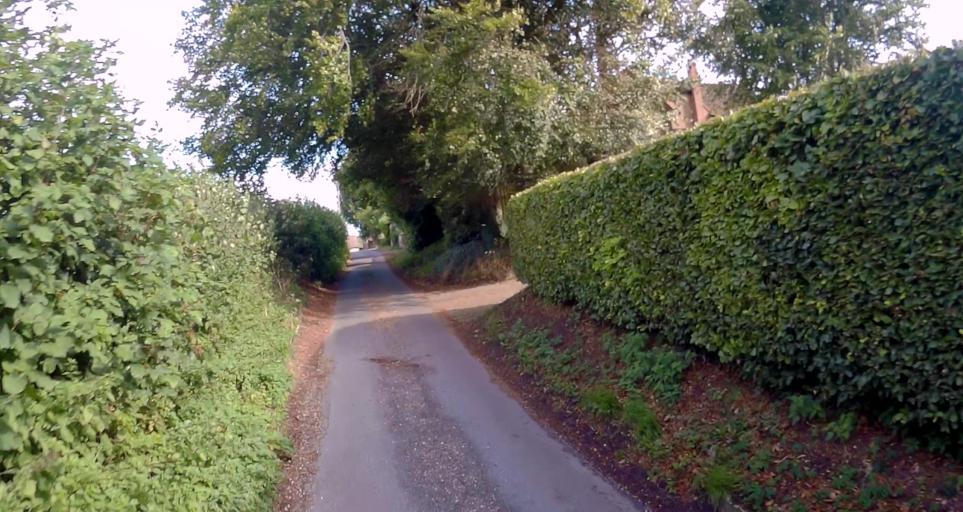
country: GB
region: England
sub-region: Hampshire
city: Kings Worthy
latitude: 51.0820
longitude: -1.2027
